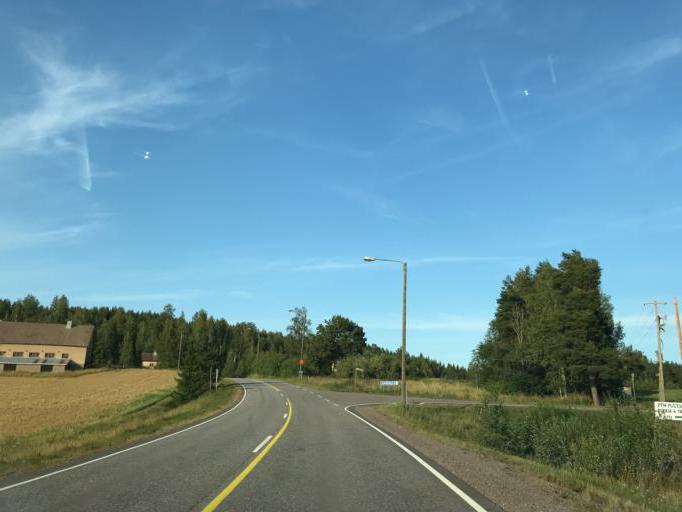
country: FI
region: Uusimaa
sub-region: Helsinki
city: Vihti
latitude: 60.4194
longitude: 24.3499
